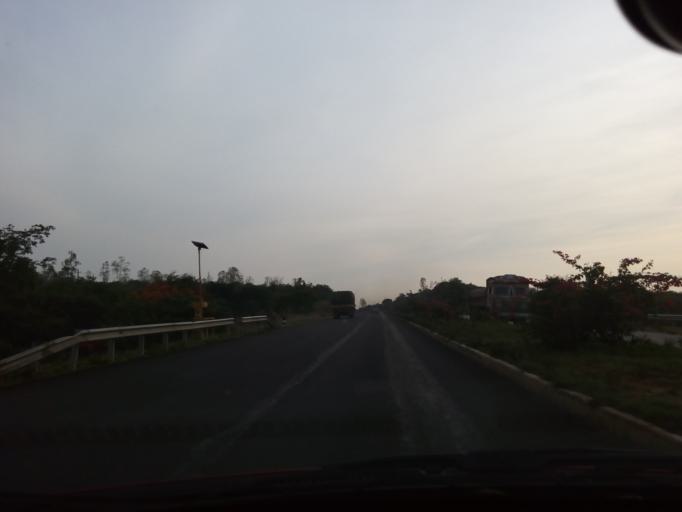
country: IN
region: Karnataka
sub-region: Chikkaballapur
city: Chik Ballapur
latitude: 13.5507
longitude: 77.7755
